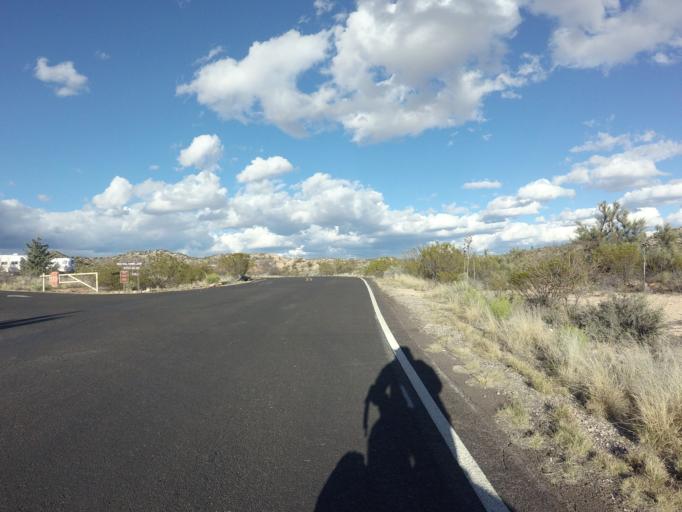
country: US
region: Arizona
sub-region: Yavapai County
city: Cottonwood
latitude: 34.7585
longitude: -112.0149
